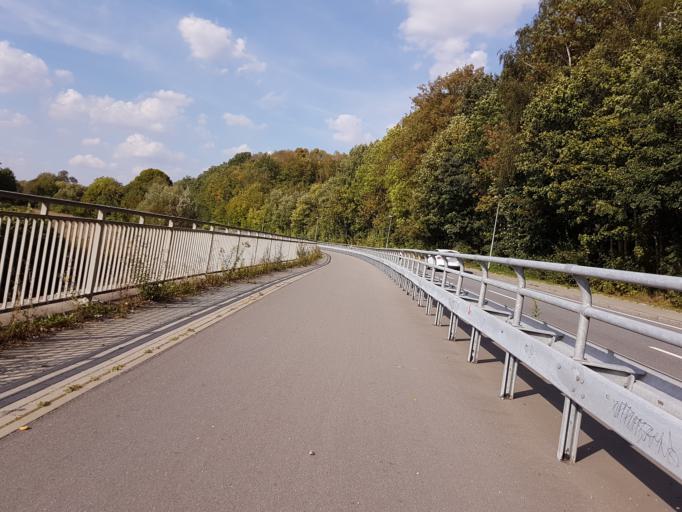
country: DE
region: Saxony
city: Taura
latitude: 50.9208
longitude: 12.8579
